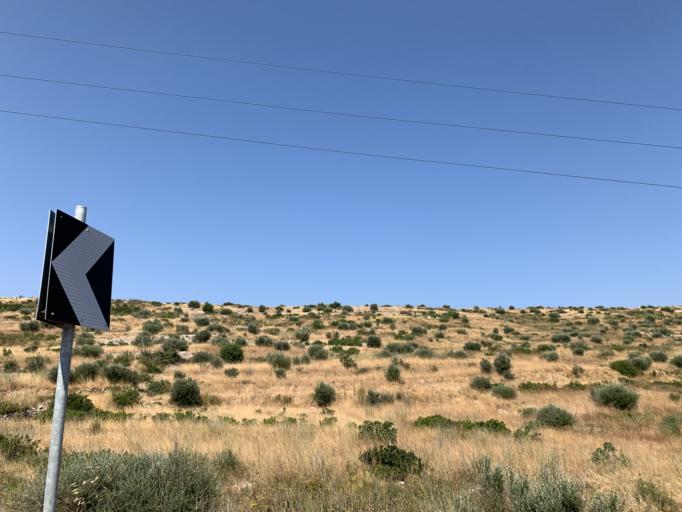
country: GR
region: North Aegean
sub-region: Chios
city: Thymiana
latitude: 38.3080
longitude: 26.0008
